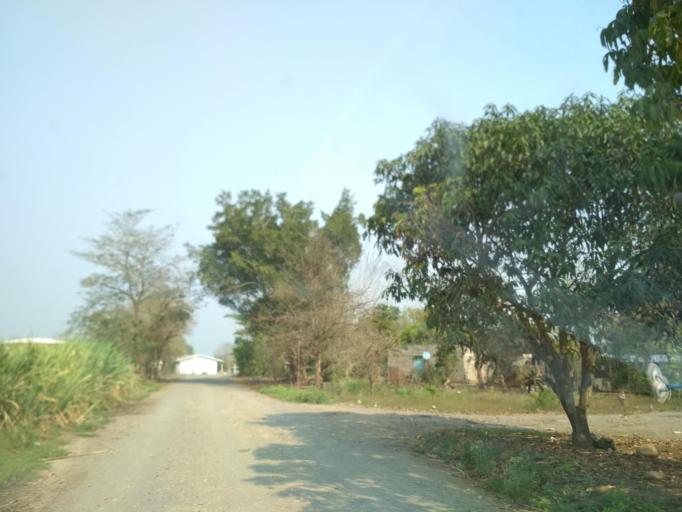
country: MX
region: Oaxaca
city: Acatlan de Perez Figueroa
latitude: 18.6048
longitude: -96.5735
